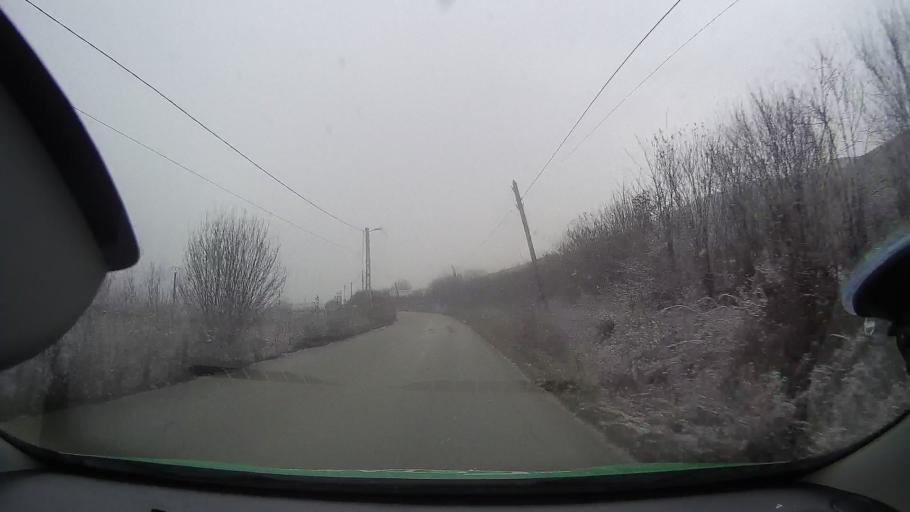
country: RO
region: Alba
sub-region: Comuna Farau
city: Farau
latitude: 46.3381
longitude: 23.9536
